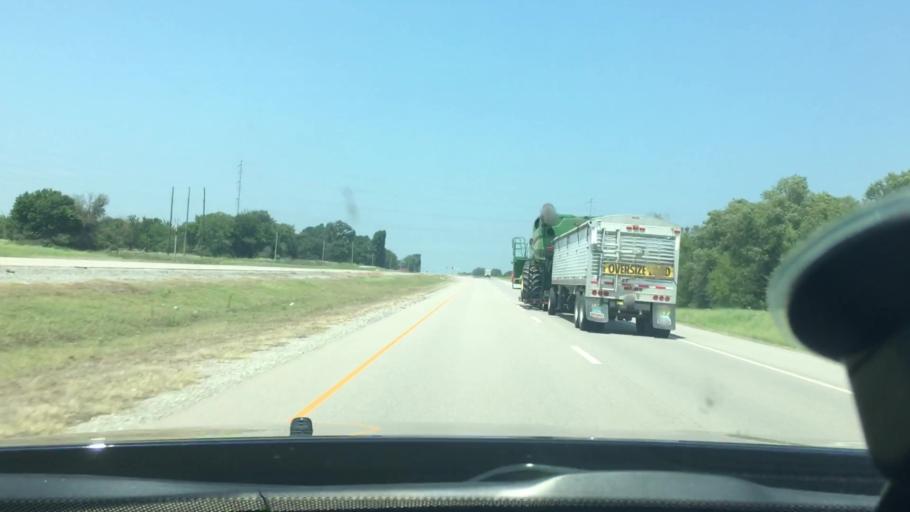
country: US
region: Oklahoma
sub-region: Atoka County
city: Atoka
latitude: 34.3288
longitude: -96.0473
